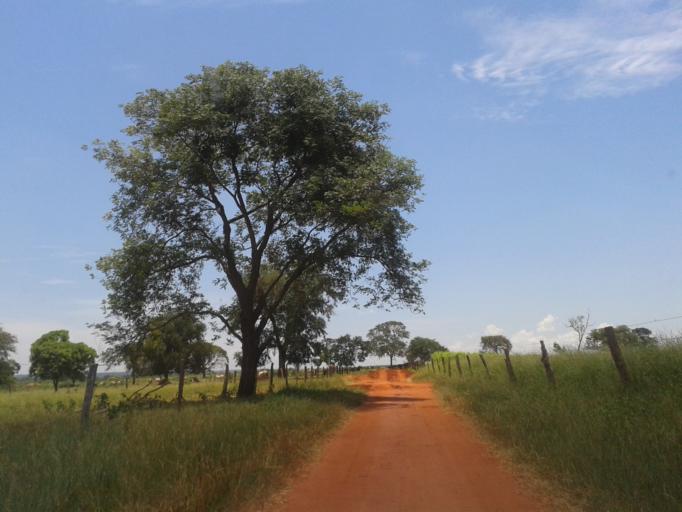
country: BR
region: Minas Gerais
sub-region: Santa Vitoria
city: Santa Vitoria
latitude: -19.2268
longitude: -50.4763
